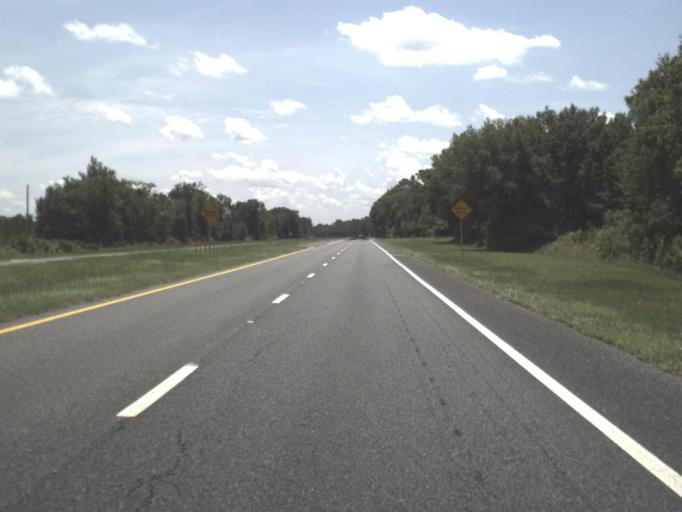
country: US
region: Florida
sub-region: Taylor County
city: Steinhatchee
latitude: 29.7406
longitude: -83.3183
